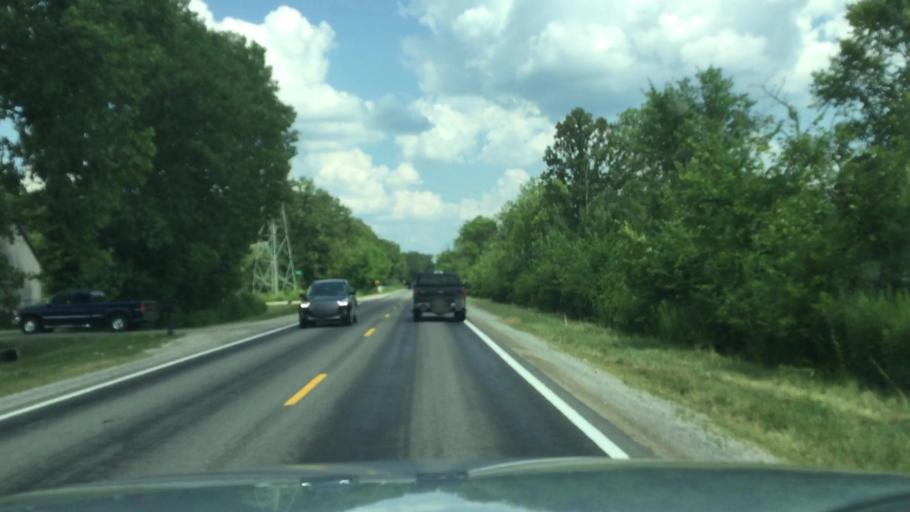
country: US
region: Michigan
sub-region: Washtenaw County
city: Ypsilanti
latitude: 42.2032
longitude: -83.5957
